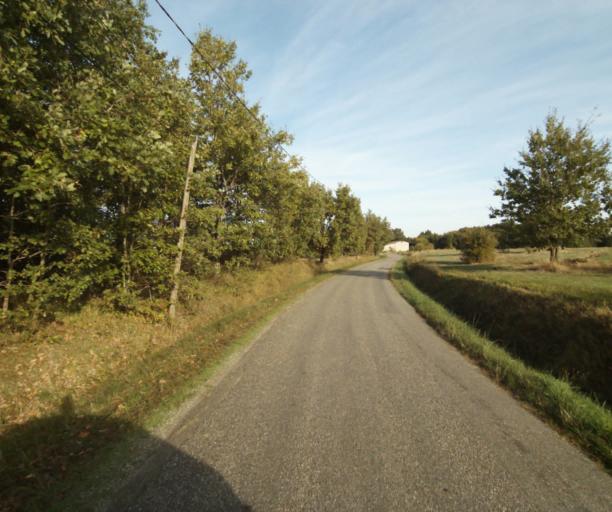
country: FR
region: Midi-Pyrenees
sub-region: Departement de la Haute-Garonne
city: Villemur-sur-Tarn
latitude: 43.9130
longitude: 1.5106
